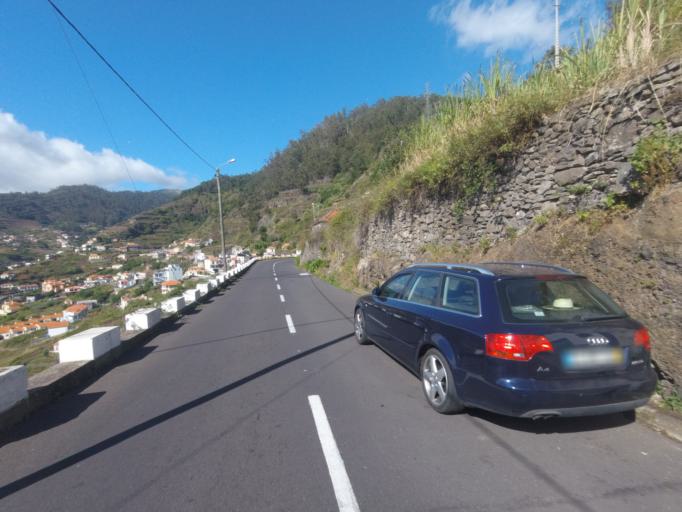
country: PT
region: Madeira
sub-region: Ribeira Brava
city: Campanario
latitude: 32.6678
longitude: -17.0221
